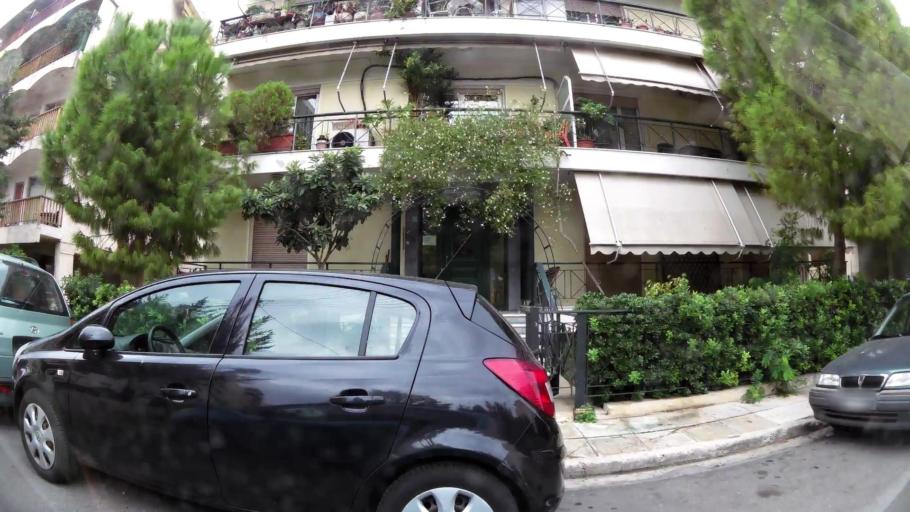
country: GR
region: Attica
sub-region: Nomarchia Athinas
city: Palaio Faliro
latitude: 37.9300
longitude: 23.7044
